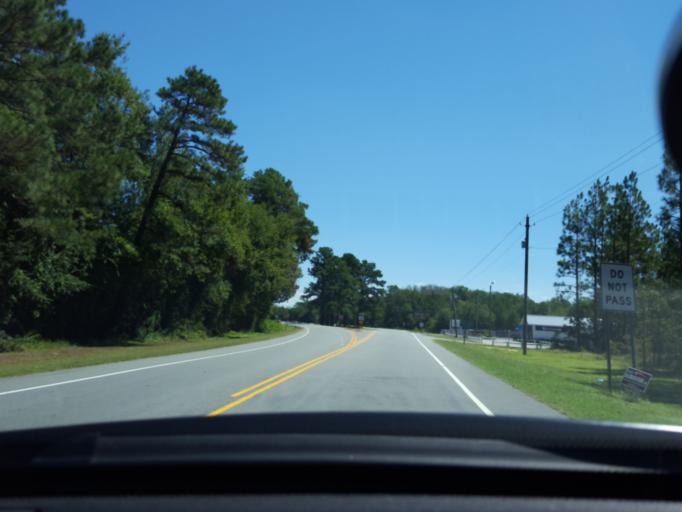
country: US
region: North Carolina
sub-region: Bladen County
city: Elizabethtown
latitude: 34.6486
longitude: -78.5296
